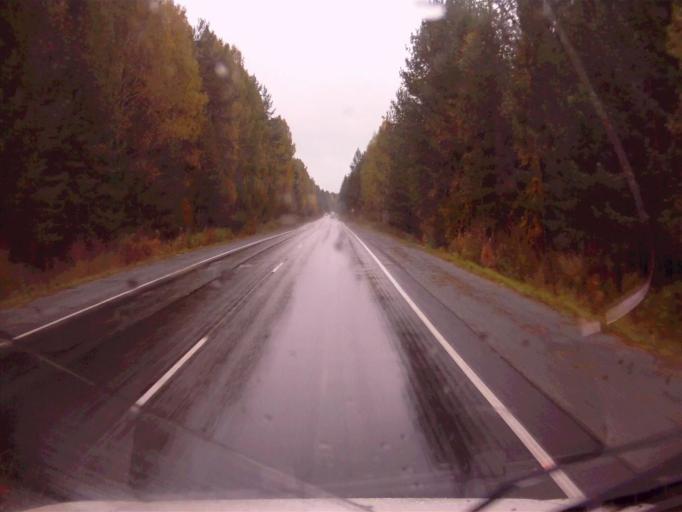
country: RU
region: Chelyabinsk
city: Tayginka
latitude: 55.5513
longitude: 60.6463
